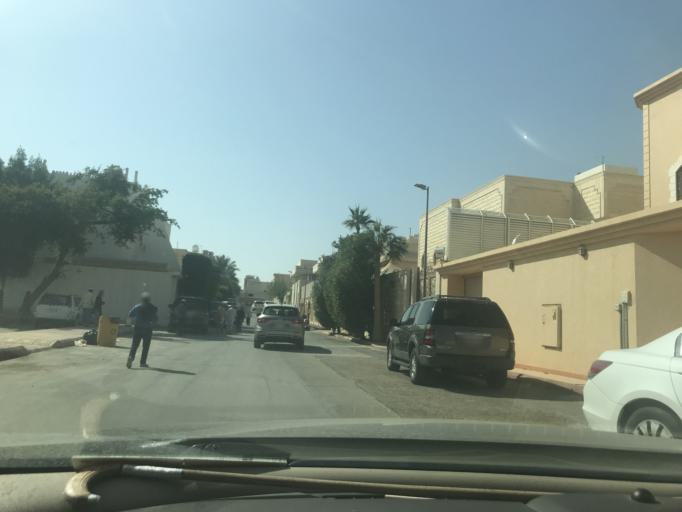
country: SA
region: Ar Riyad
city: Riyadh
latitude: 24.7343
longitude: 46.7664
